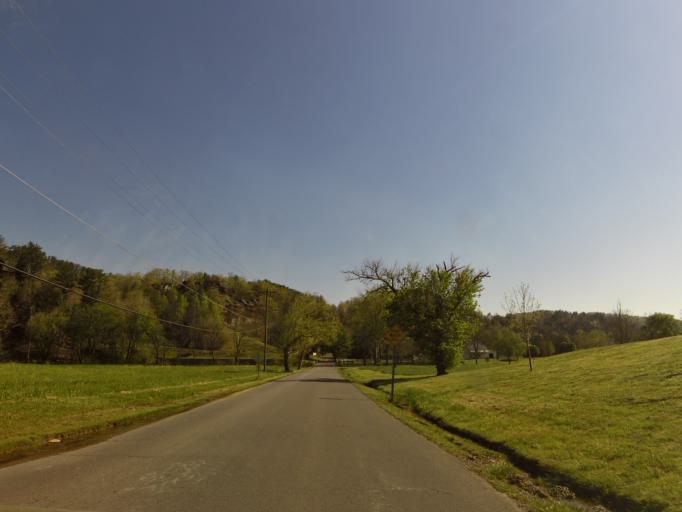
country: US
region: Tennessee
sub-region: Sevier County
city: Pigeon Forge
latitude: 35.7870
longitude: -83.6267
